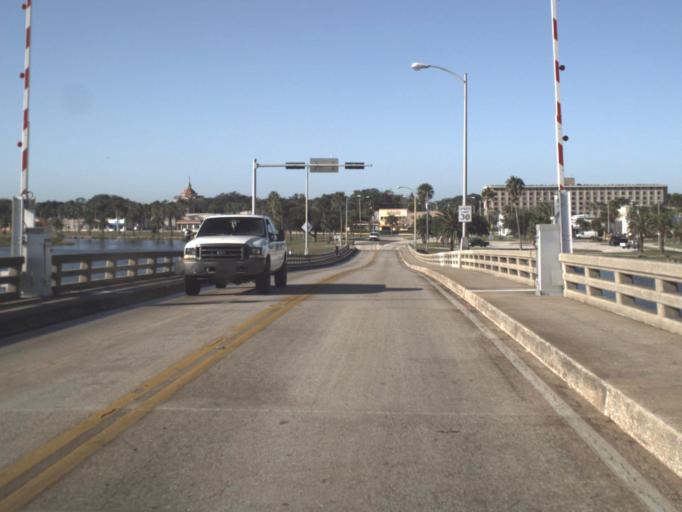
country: US
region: Florida
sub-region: Volusia County
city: Daytona Beach
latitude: 29.2225
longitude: -81.0193
